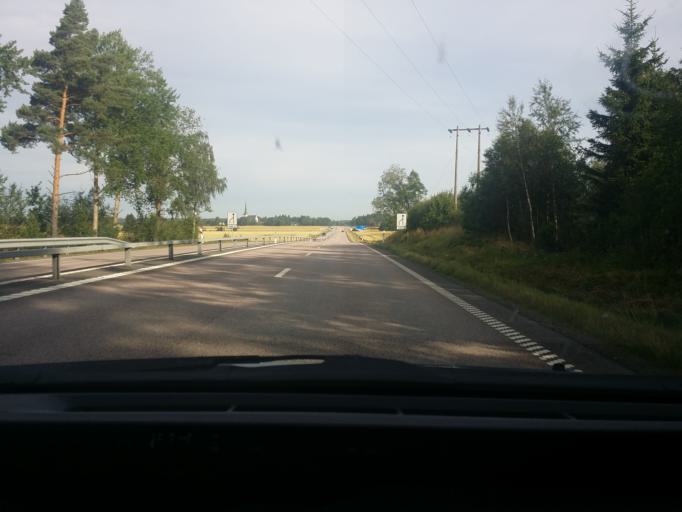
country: SE
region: Vaestmanland
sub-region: Vasteras
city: Hokasen
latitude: 59.7206
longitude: 16.5763
